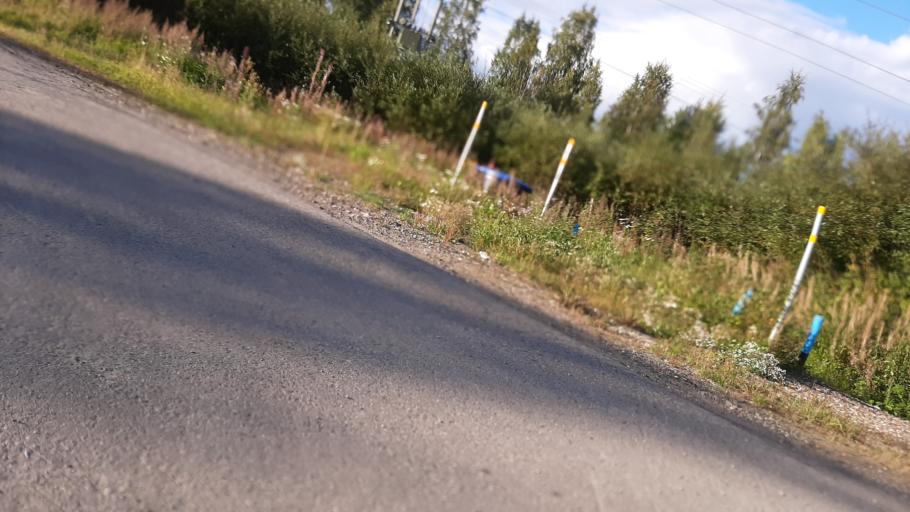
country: FI
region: North Karelia
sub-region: Joensuu
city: Joensuu
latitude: 62.6298
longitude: 29.8031
